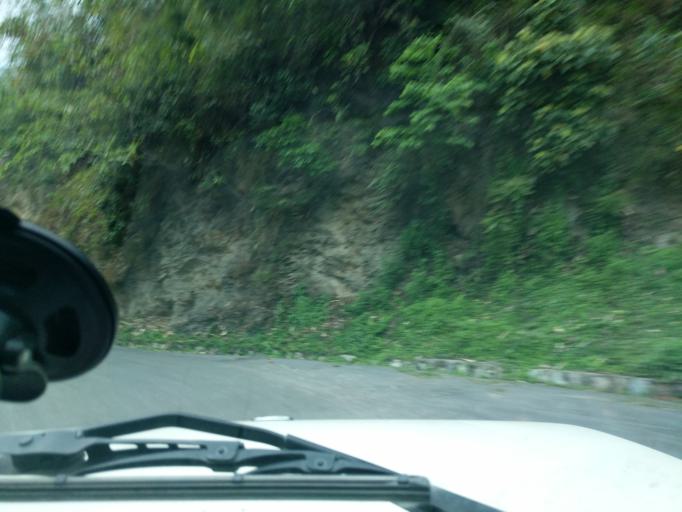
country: BT
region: Mongar
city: Mongar
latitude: 27.3029
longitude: 91.1507
